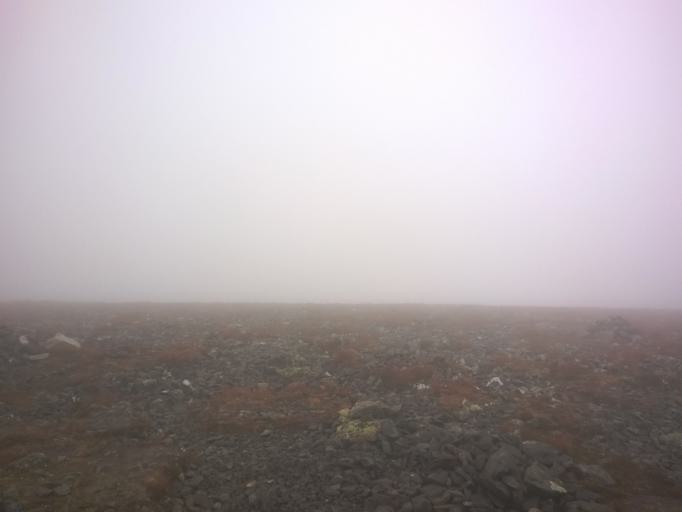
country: FI
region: Lapland
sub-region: Tunturi-Lappi
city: Muonio
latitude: 68.0536
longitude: 24.0961
